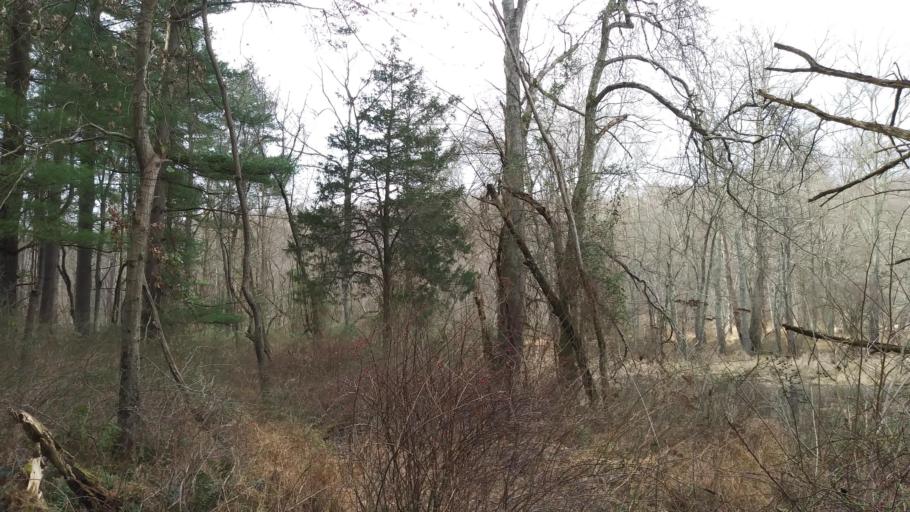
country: US
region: Pennsylvania
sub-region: York County
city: Susquehanna Trails
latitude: 39.6840
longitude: -76.2757
